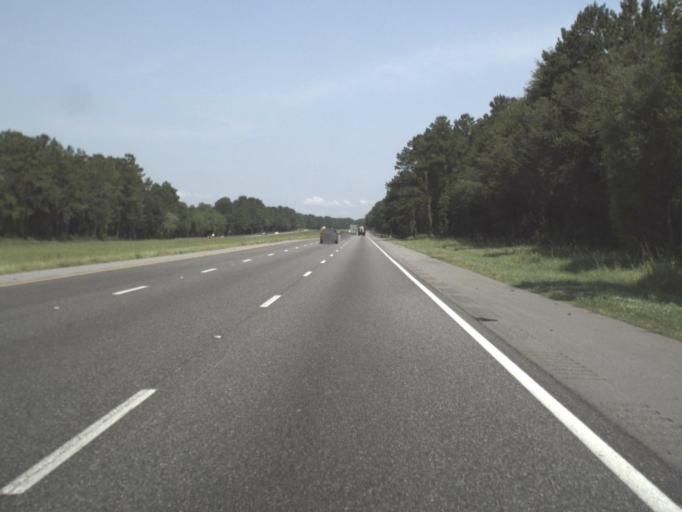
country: US
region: Florida
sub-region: Suwannee County
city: Wellborn
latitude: 30.3587
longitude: -82.8435
